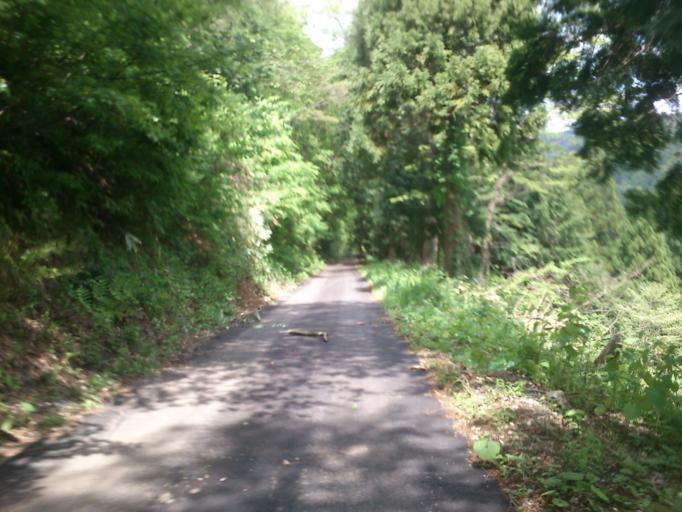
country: JP
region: Kyoto
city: Miyazu
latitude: 35.6475
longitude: 135.1561
